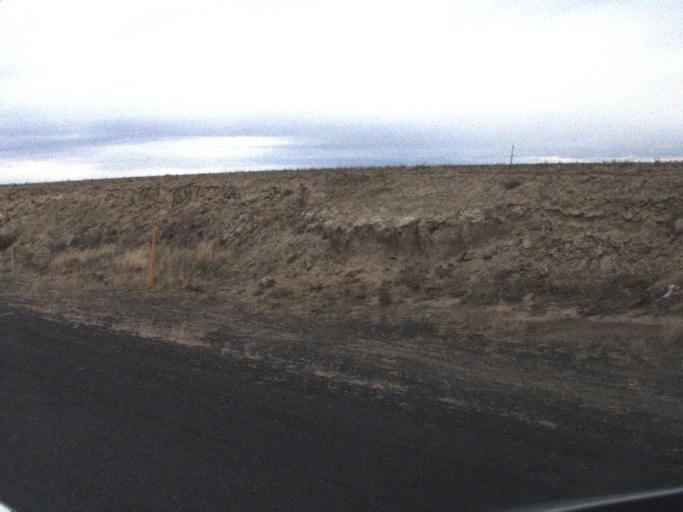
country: US
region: Washington
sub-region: Franklin County
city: Connell
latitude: 46.7945
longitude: -118.6407
